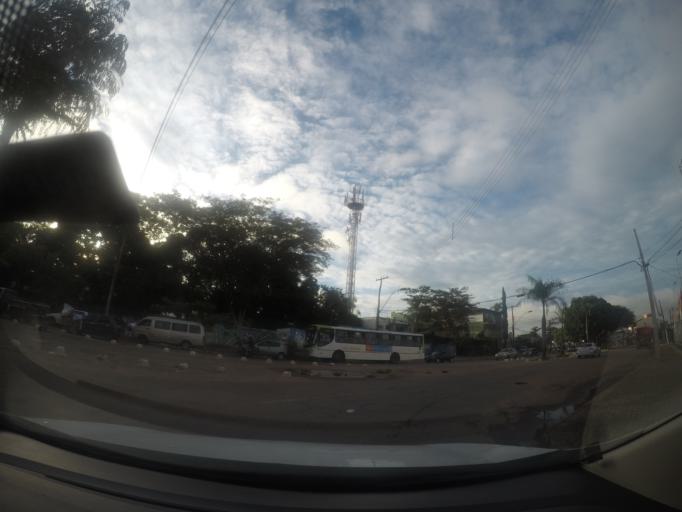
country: BR
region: Goias
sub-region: Goiania
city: Goiania
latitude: -16.6820
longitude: -49.3106
